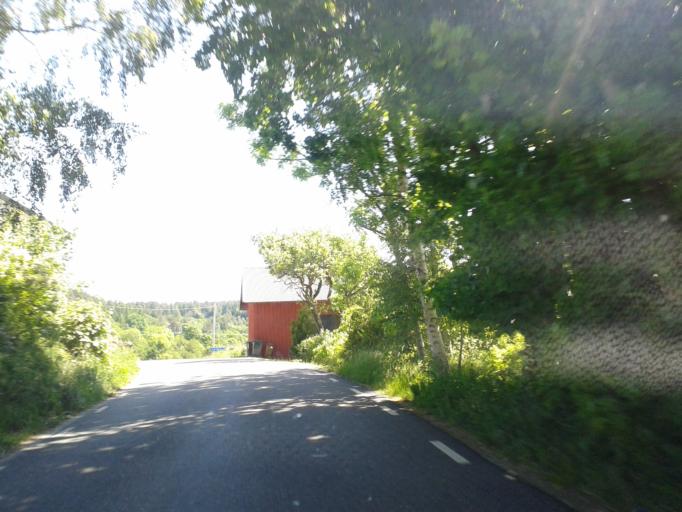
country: SE
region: Vaestra Goetaland
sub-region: Stenungsunds Kommun
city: Stora Hoga
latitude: 58.0233
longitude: 11.8779
